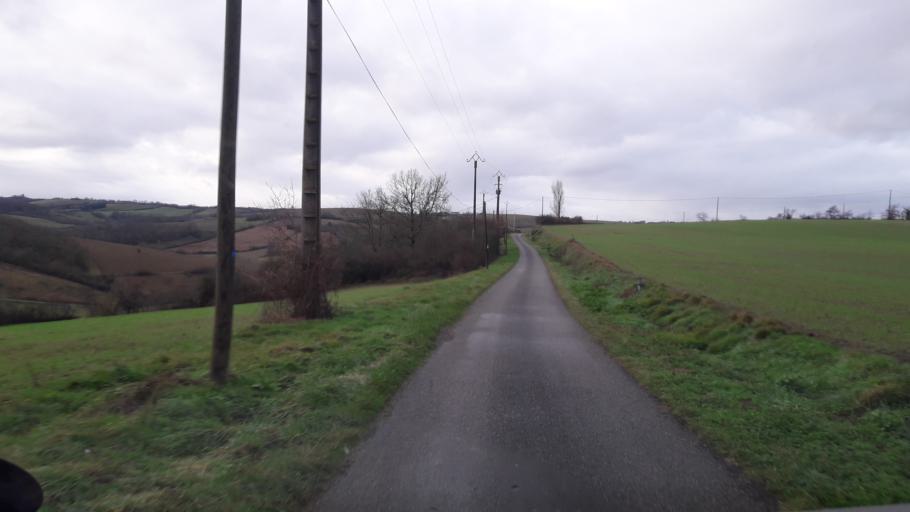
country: FR
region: Midi-Pyrenees
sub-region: Departement de la Haute-Garonne
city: Carbonne
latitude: 43.2560
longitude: 1.2580
